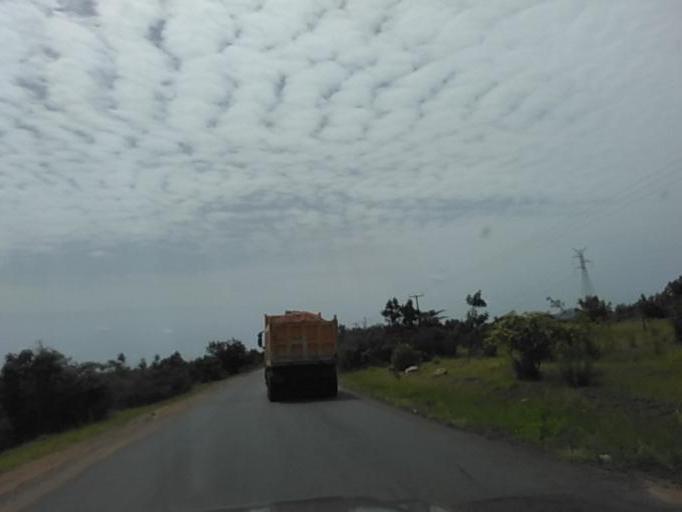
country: GH
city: Akropong
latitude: 6.0950
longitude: 0.0528
